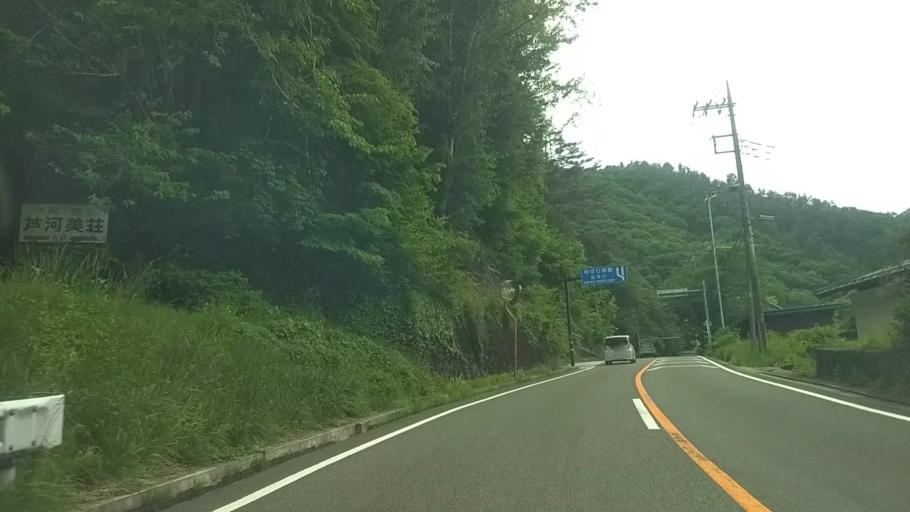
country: JP
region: Yamanashi
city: Fujikawaguchiko
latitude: 35.5284
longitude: 138.6247
